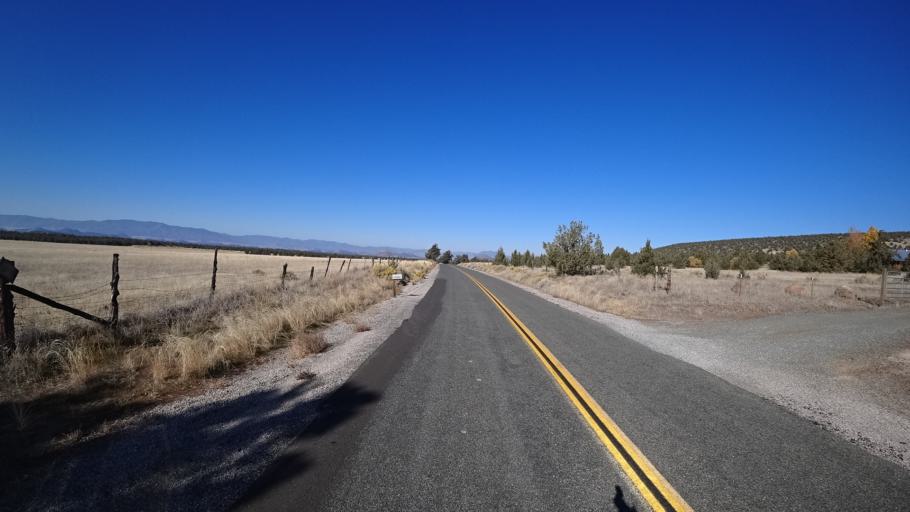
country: US
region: California
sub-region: Siskiyou County
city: Weed
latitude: 41.6124
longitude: -122.3140
